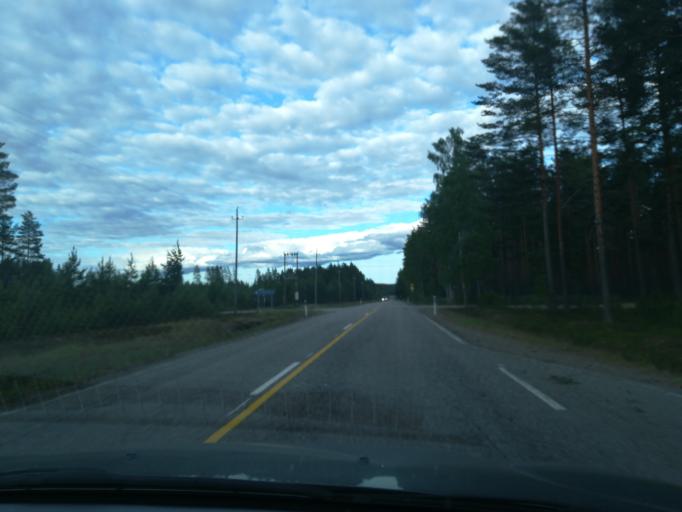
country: FI
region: Southern Savonia
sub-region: Mikkeli
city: Puumala
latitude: 61.5603
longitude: 28.0085
